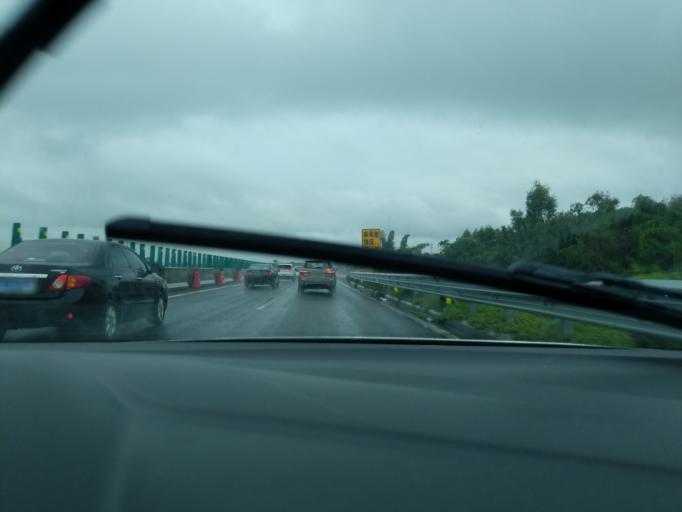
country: CN
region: Guangdong
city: Yueshan
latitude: 22.4648
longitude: 112.7053
